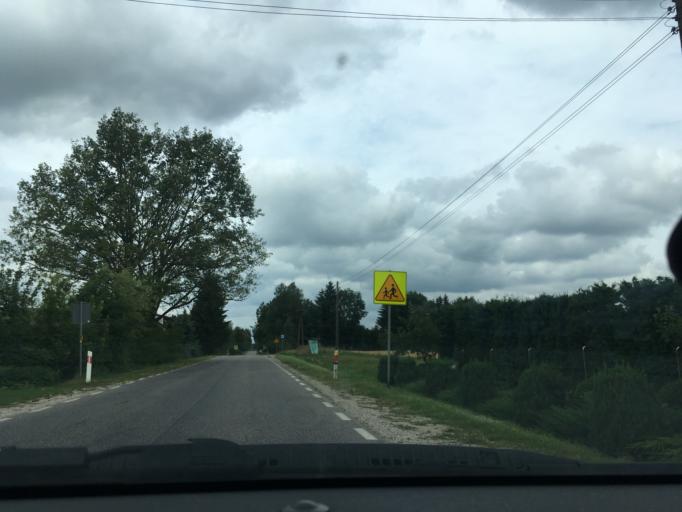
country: PL
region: Podlasie
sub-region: Powiat suwalski
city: Raczki
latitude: 53.9499
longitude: 22.8295
